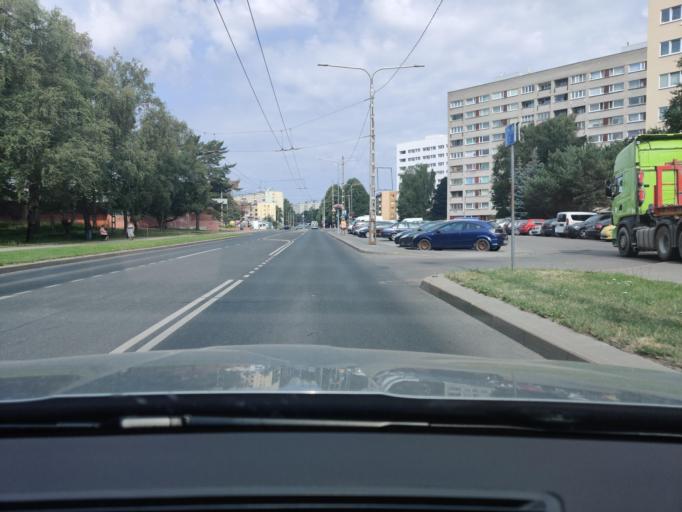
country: EE
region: Harju
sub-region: Tallinna linn
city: Tallinn
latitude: 59.4026
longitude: 24.6895
